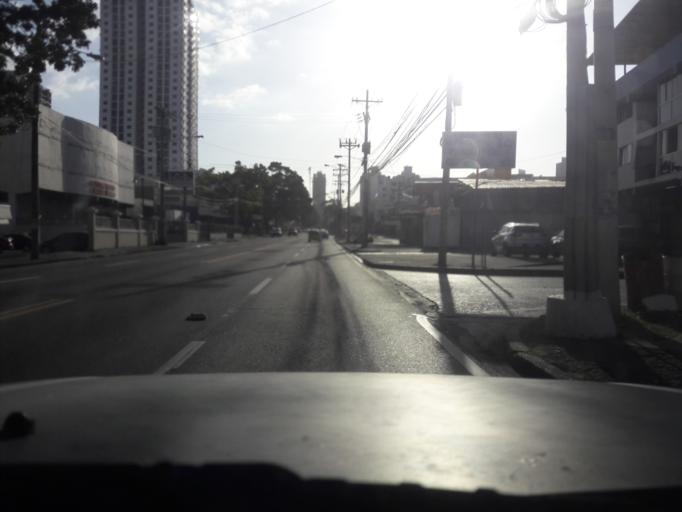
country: PA
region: Panama
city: Panama
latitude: 9.0126
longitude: -79.5020
